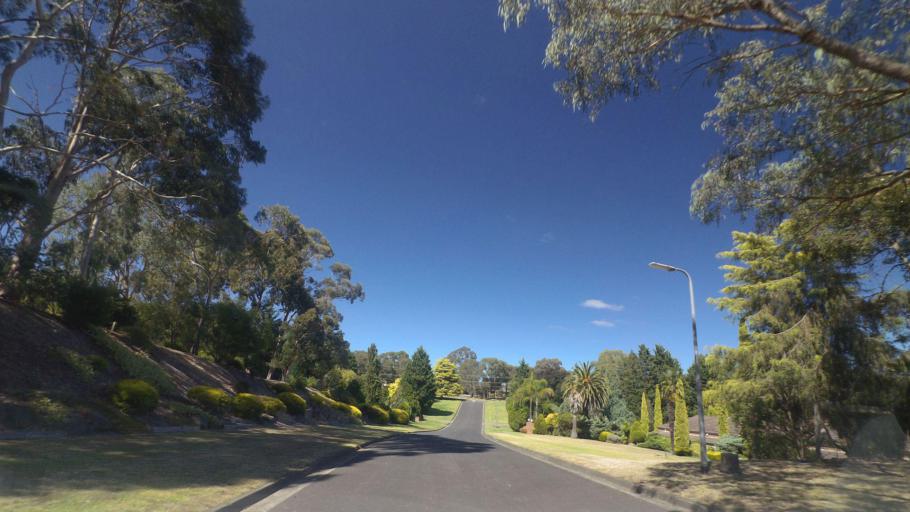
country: AU
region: Victoria
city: Mitcham
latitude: -37.8033
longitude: 145.2088
